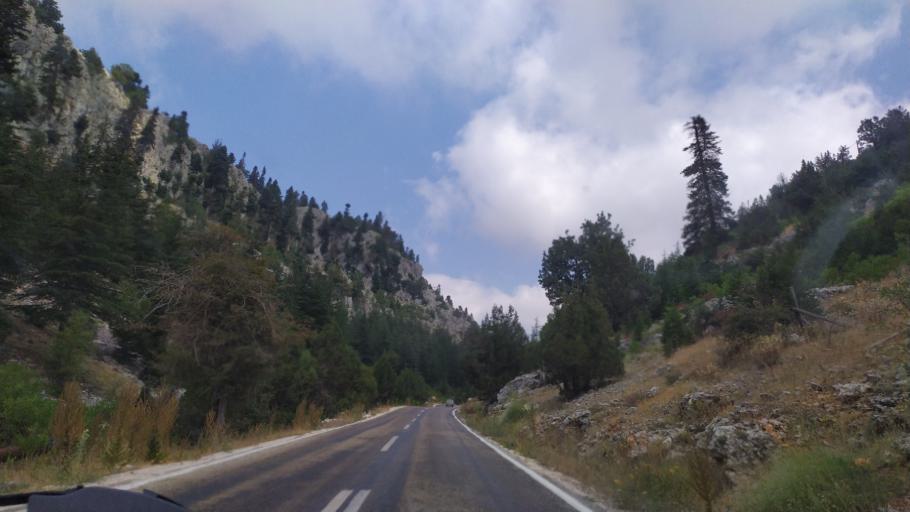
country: TR
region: Mersin
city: Kirobasi
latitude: 36.6086
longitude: 33.8829
